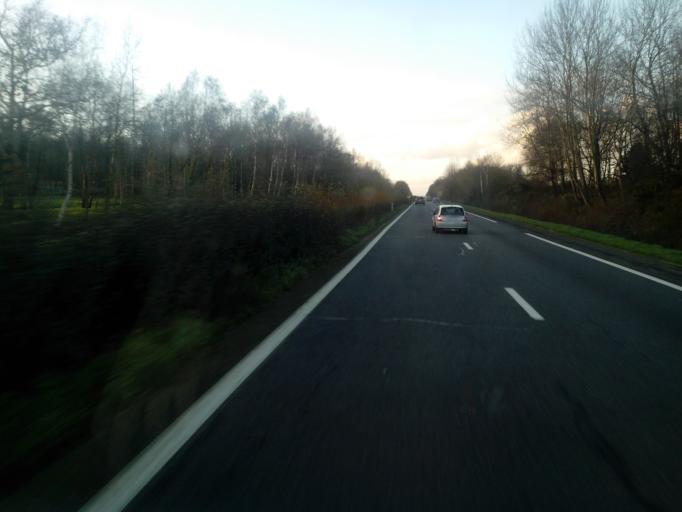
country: FR
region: Pays de la Loire
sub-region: Departement de la Loire-Atlantique
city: Haute-Goulaine
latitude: 47.1852
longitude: -1.4199
